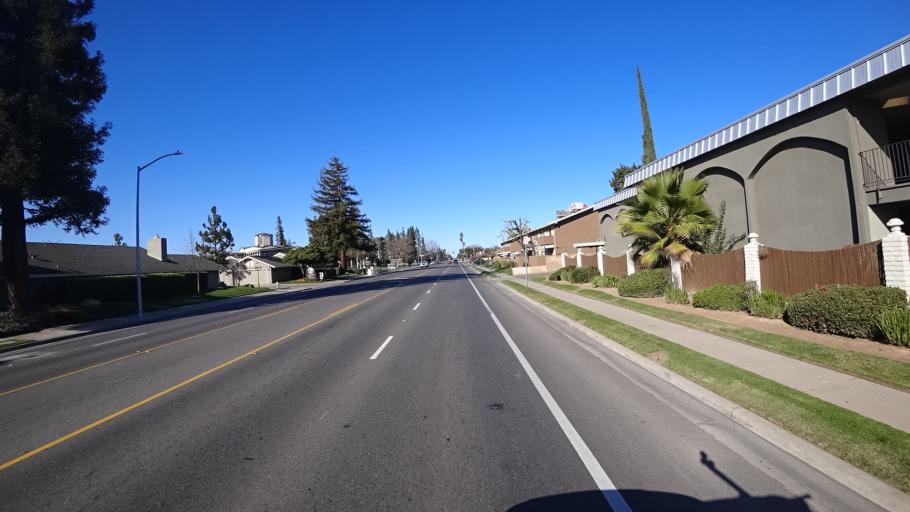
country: US
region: California
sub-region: Fresno County
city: Fresno
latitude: 36.8230
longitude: -119.7970
